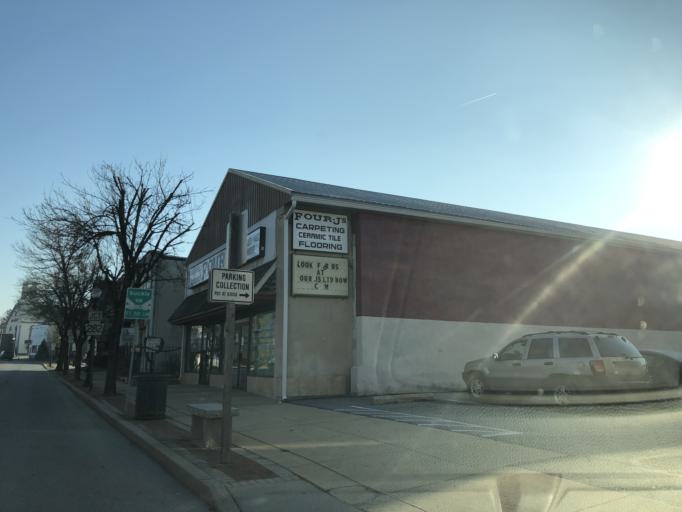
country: US
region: Pennsylvania
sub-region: Chester County
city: Downingtown
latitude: 40.0068
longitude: -75.7024
